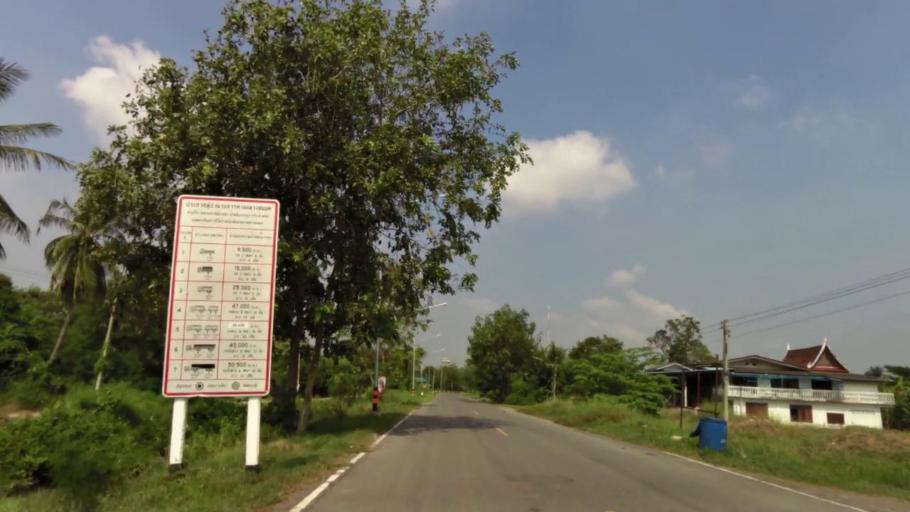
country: TH
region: Ang Thong
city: Ang Thong
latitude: 14.6039
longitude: 100.3967
